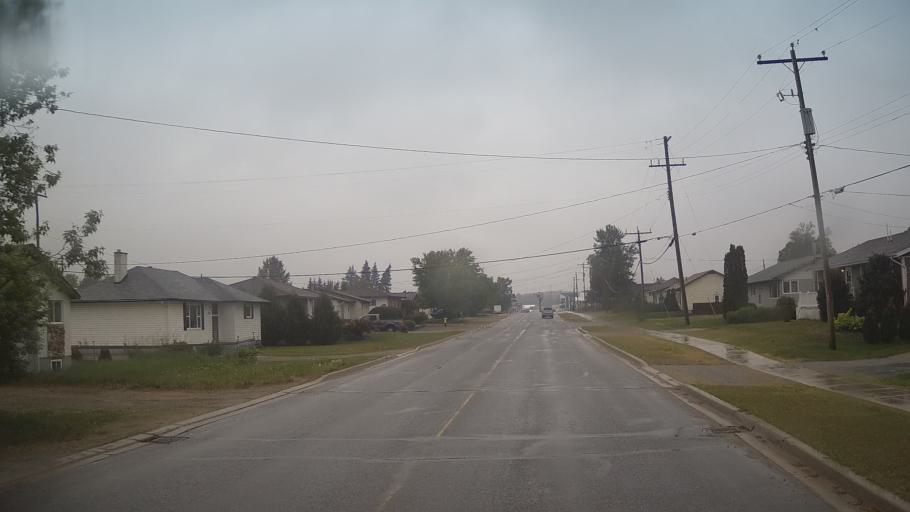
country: CA
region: Ontario
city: Greenstone
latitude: 49.7769
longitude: -86.5357
